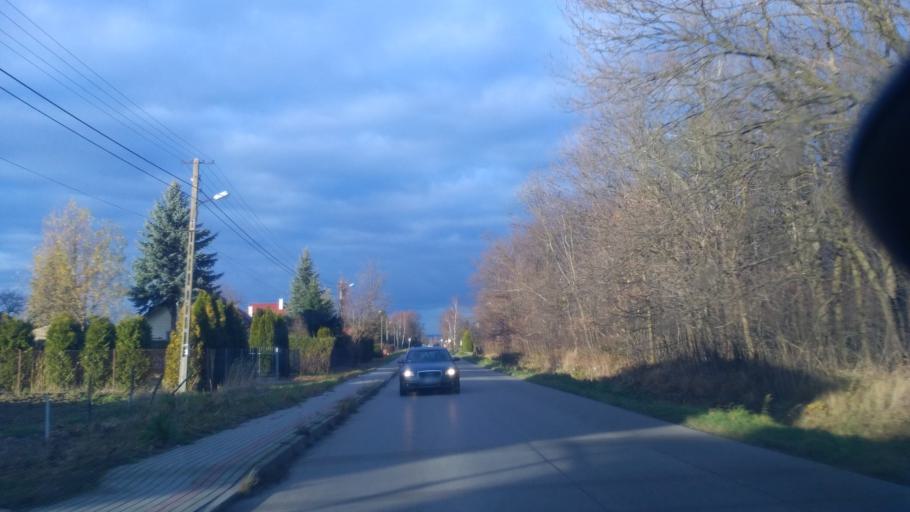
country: PL
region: Subcarpathian Voivodeship
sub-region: Powiat rzeszowski
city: Krasne
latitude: 50.0509
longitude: 22.1223
